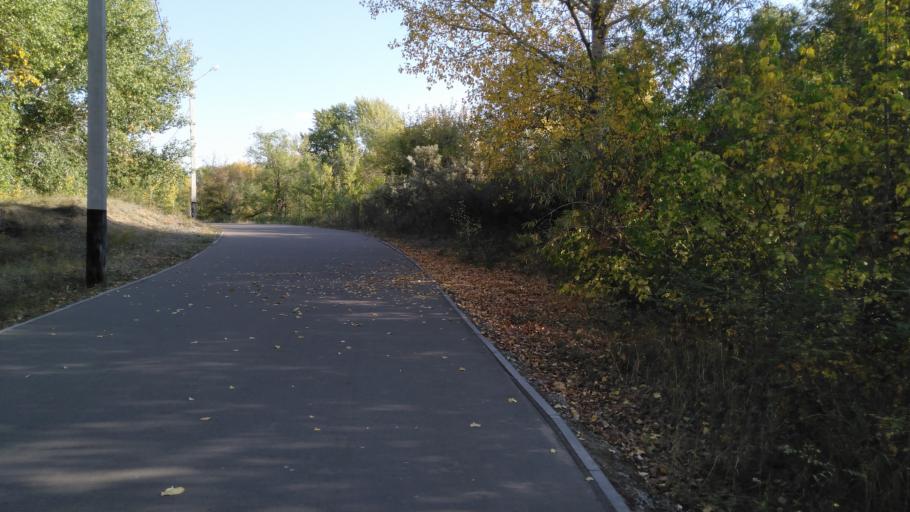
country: KZ
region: Pavlodar
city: Pavlodar
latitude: 52.2627
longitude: 76.9318
